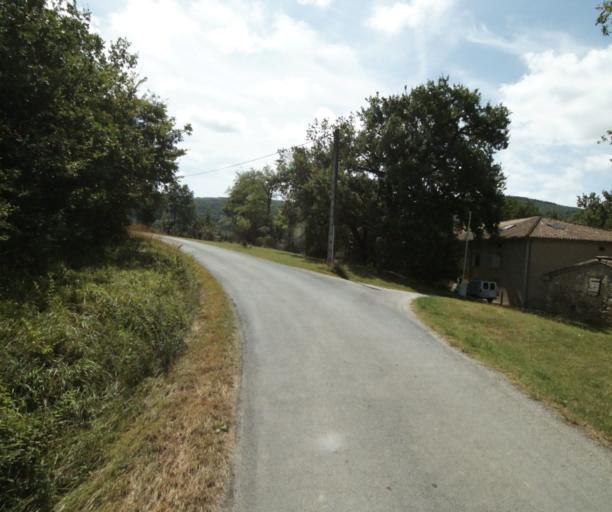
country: FR
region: Midi-Pyrenees
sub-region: Departement du Tarn
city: Dourgne
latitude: 43.4758
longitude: 2.1113
